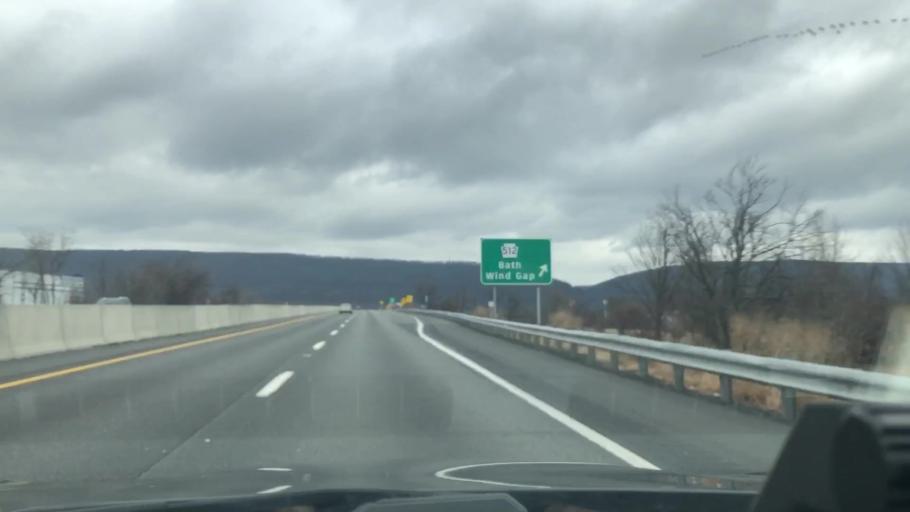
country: US
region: Pennsylvania
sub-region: Northampton County
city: Wind Gap
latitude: 40.8290
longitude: -75.2982
